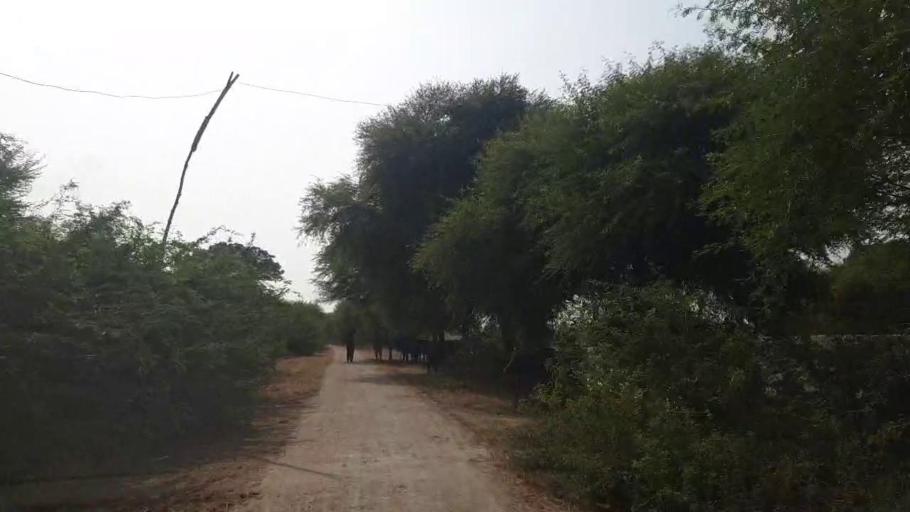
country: PK
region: Sindh
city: Badin
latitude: 24.7357
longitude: 68.7350
